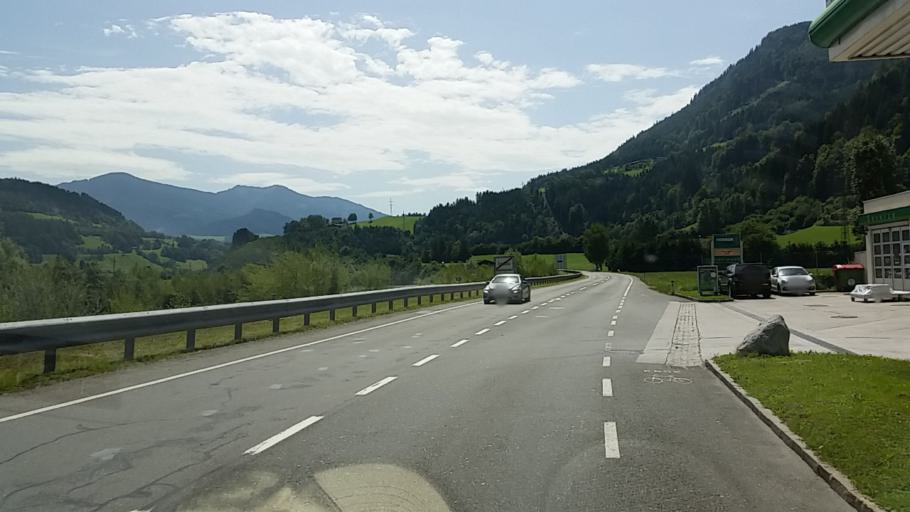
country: AT
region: Salzburg
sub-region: Politischer Bezirk Sankt Johann im Pongau
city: Pfarrwerfen
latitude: 47.4602
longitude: 13.1989
